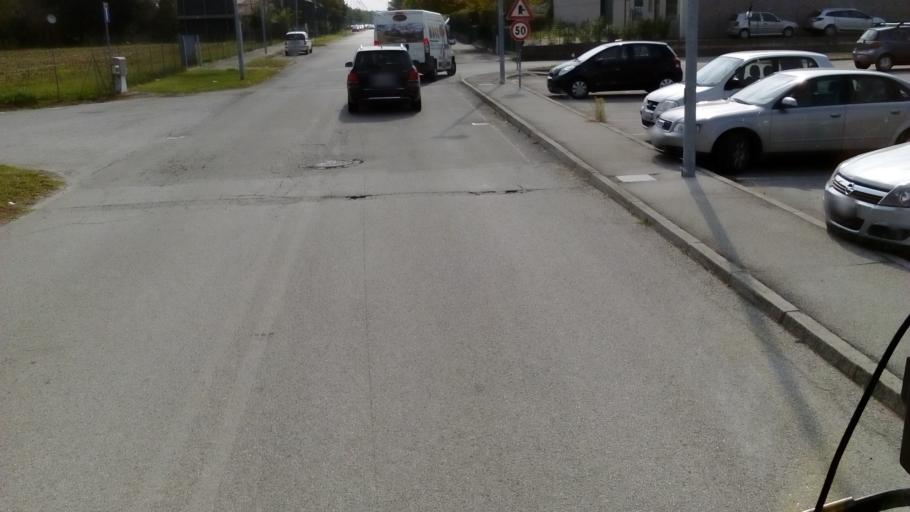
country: IT
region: Veneto
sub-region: Provincia di Padova
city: Tribano
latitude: 45.2137
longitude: 11.8455
